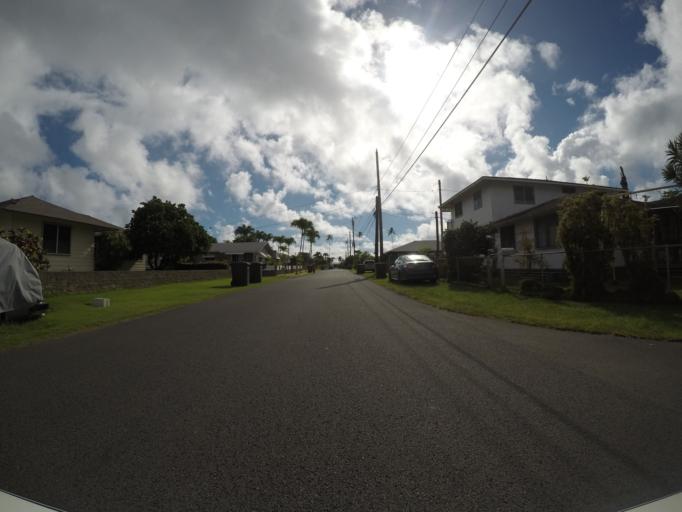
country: US
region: Hawaii
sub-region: Honolulu County
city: Kailua
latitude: 21.4009
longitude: -157.7458
